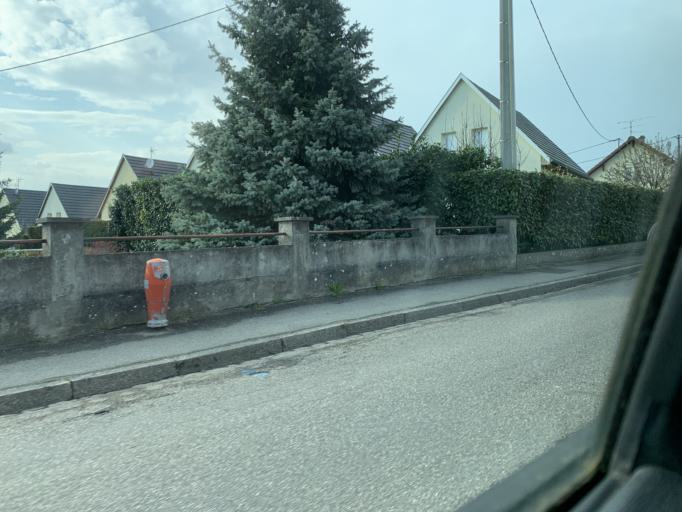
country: FR
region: Alsace
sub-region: Departement du Haut-Rhin
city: Heimsbrunn
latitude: 47.7241
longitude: 7.2259
